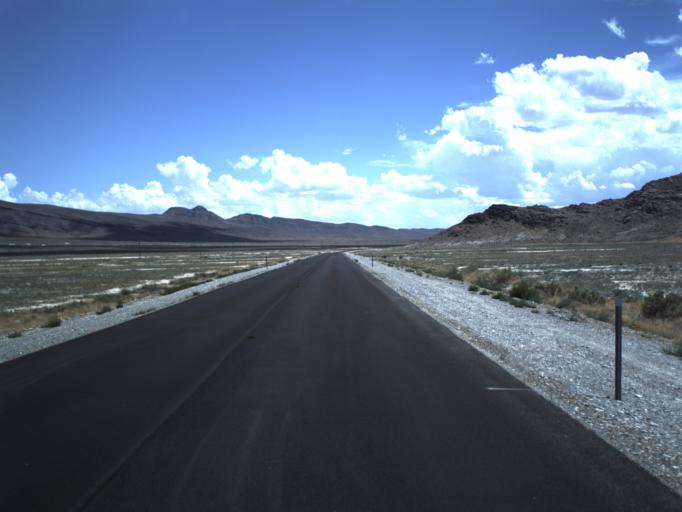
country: US
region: Utah
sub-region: Beaver County
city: Milford
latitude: 39.0670
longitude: -113.4525
